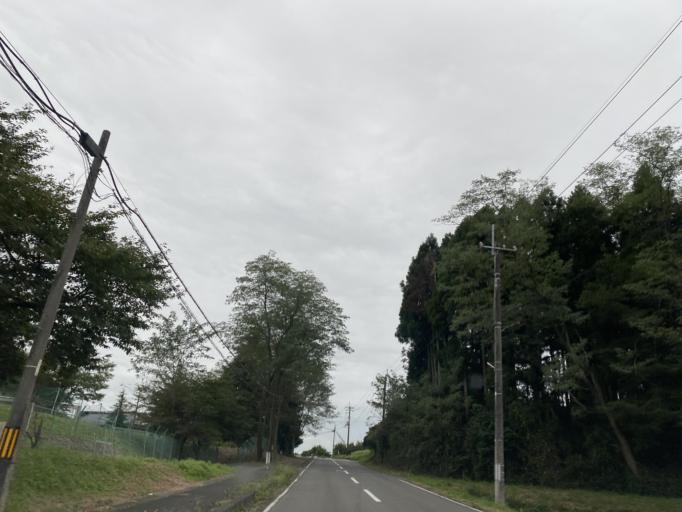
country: JP
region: Fukushima
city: Sukagawa
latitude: 37.2657
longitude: 140.3223
